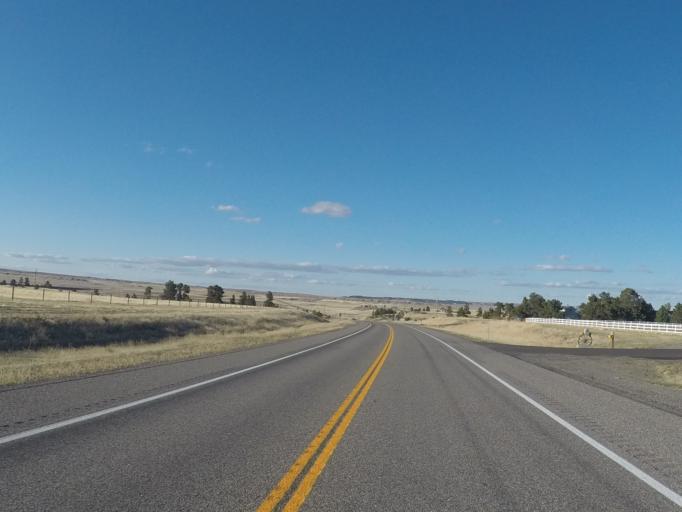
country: US
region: Montana
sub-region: Yellowstone County
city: Billings
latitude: 45.8284
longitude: -108.6362
